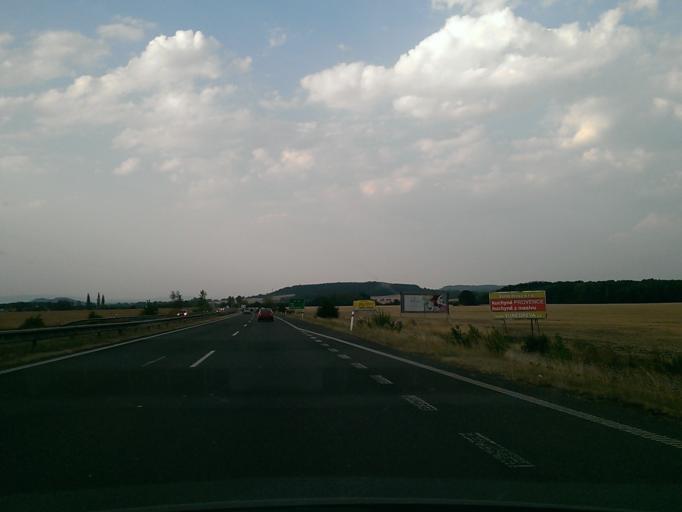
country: CZ
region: Central Bohemia
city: Bakov nad Jizerou
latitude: 50.4857
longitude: 14.9686
